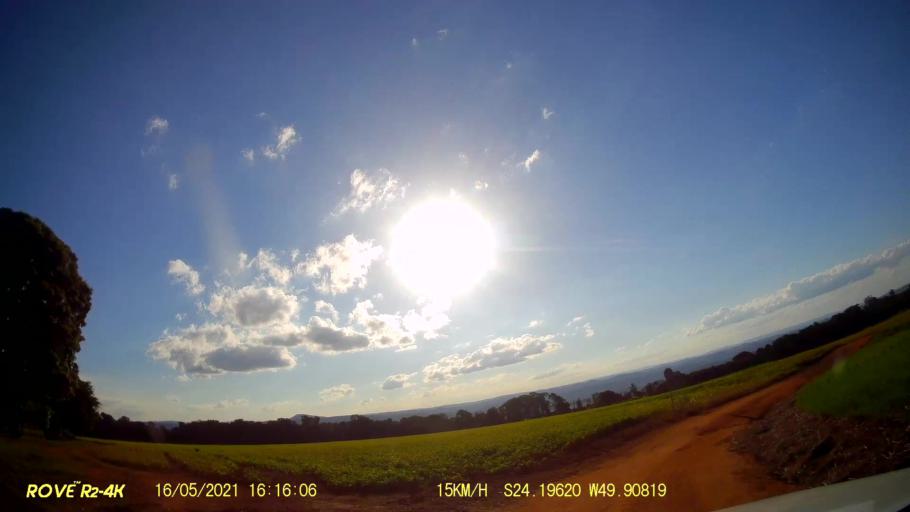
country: BR
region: Parana
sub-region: Jaguariaiva
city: Jaguariaiva
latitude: -24.1963
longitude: -49.9080
